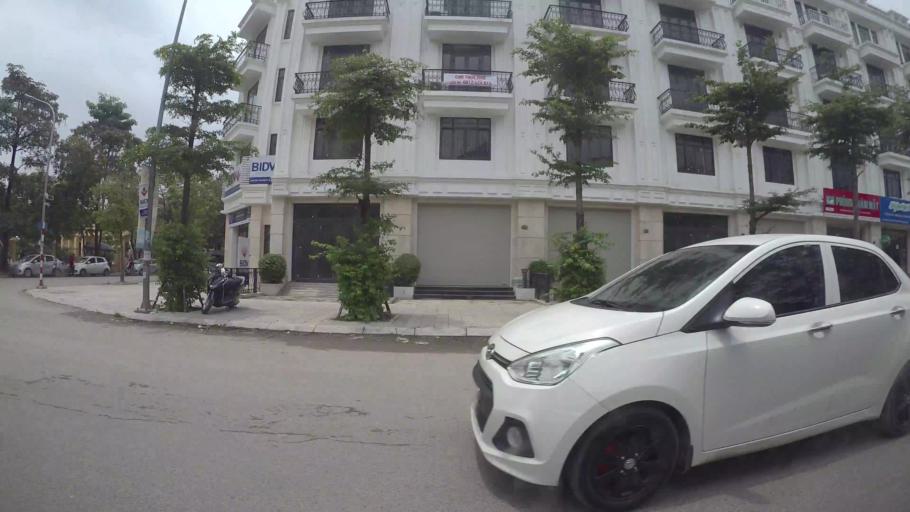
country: VN
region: Ha Noi
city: Tay Ho
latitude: 21.0672
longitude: 105.8039
